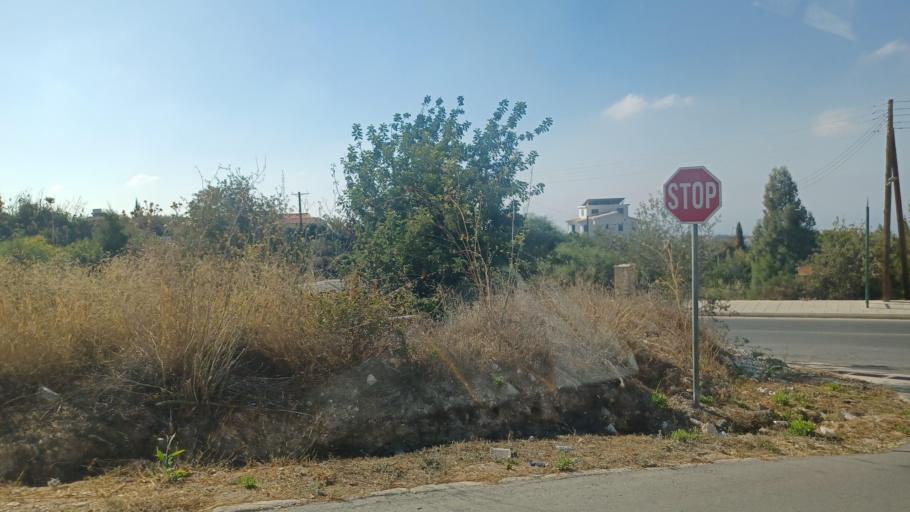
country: CY
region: Pafos
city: Tala
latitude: 34.8336
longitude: 32.4463
